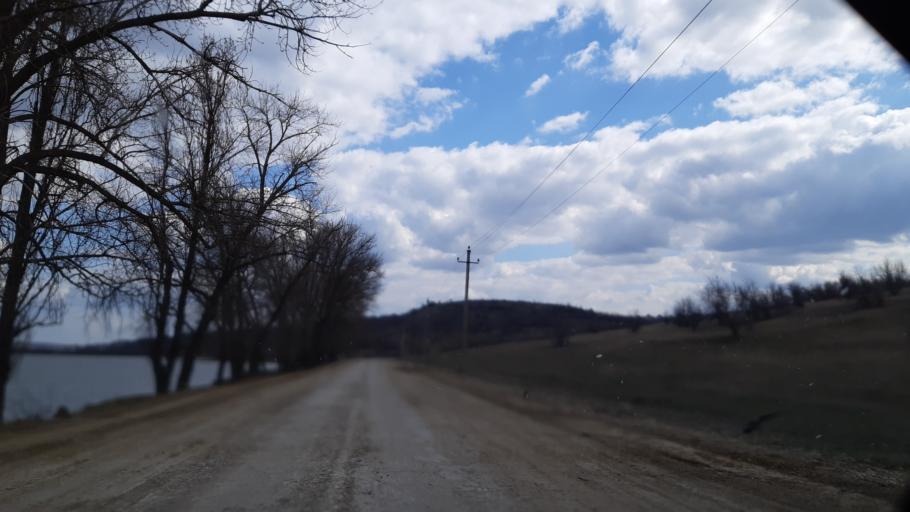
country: MD
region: Laloveni
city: Ialoveni
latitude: 46.8815
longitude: 28.7402
